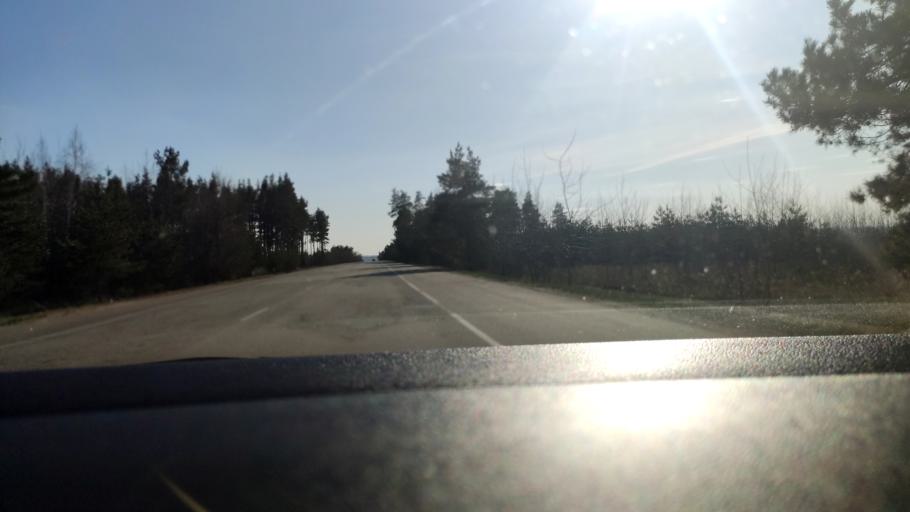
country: RU
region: Voronezj
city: Kolodeznyy
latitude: 51.3671
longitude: 39.1982
